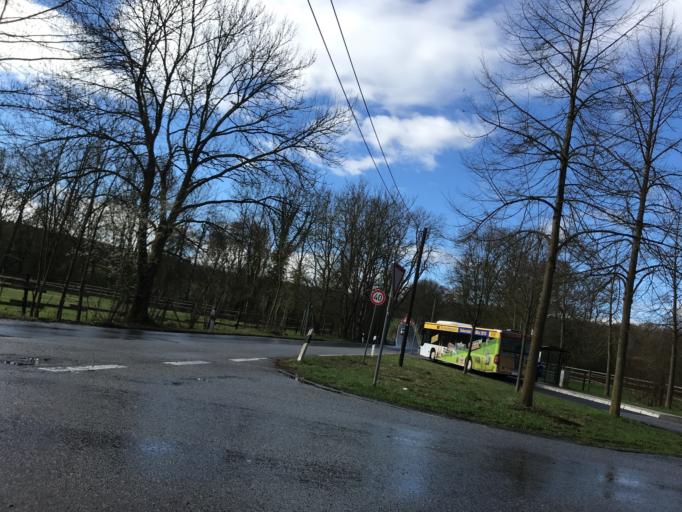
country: DE
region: Hesse
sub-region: Regierungsbezirk Darmstadt
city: Wiesbaden
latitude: 50.1021
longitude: 8.1917
